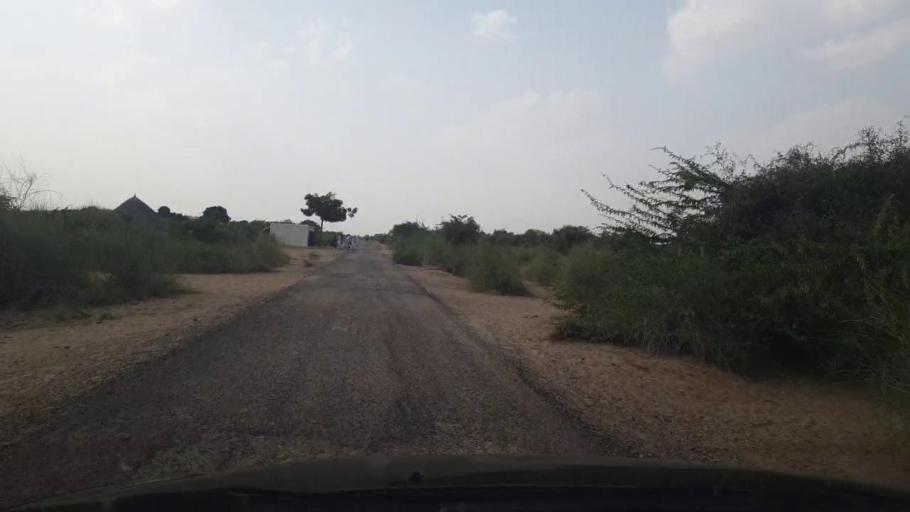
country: PK
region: Sindh
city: Islamkot
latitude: 24.9865
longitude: 70.5768
